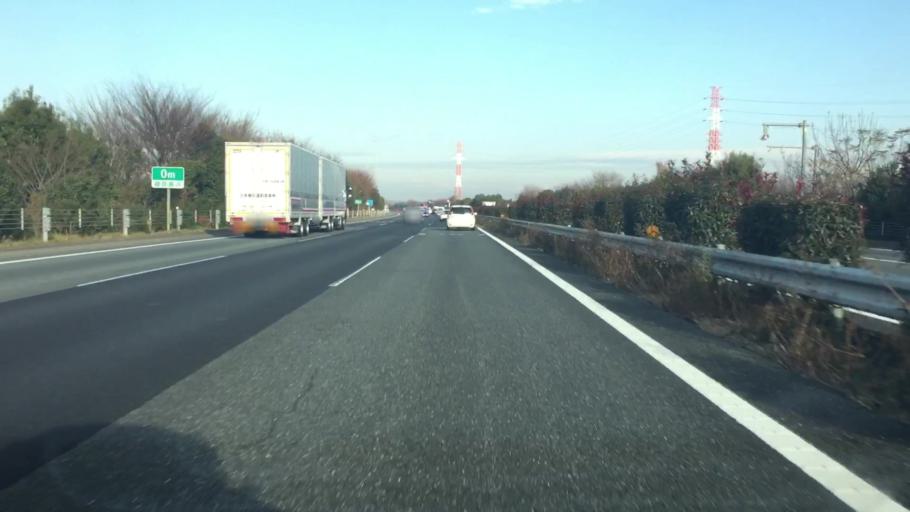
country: JP
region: Saitama
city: Yorii
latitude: 36.1466
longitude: 139.2222
